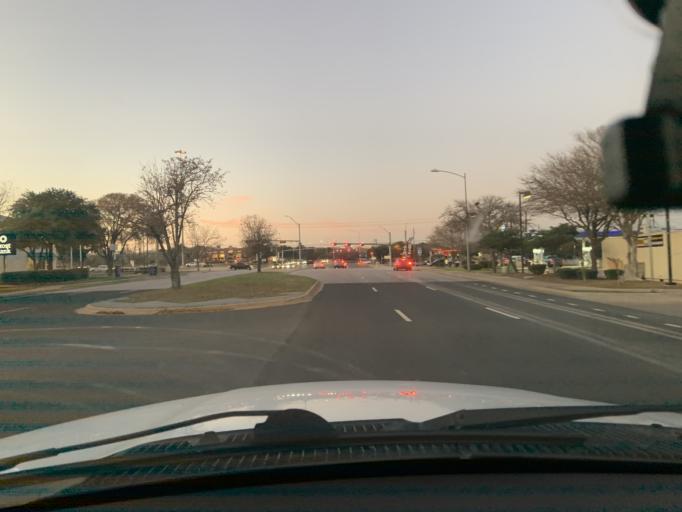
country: US
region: Texas
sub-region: Williamson County
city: Anderson Mill
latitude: 30.4649
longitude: -97.8035
